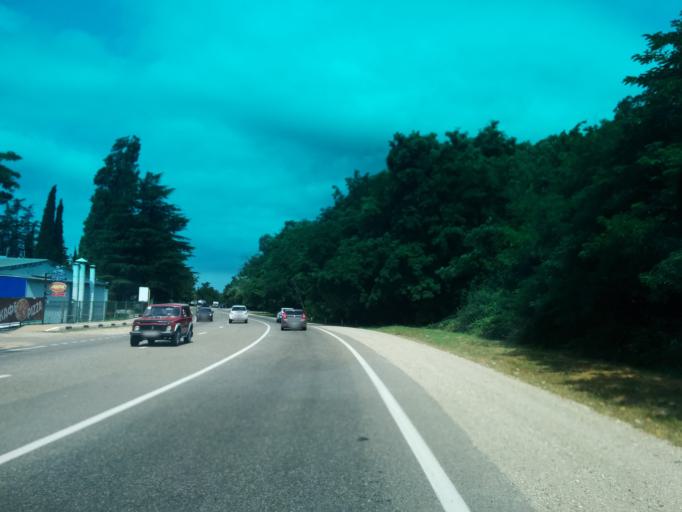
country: RU
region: Krasnodarskiy
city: Nebug
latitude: 44.1700
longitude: 38.9834
